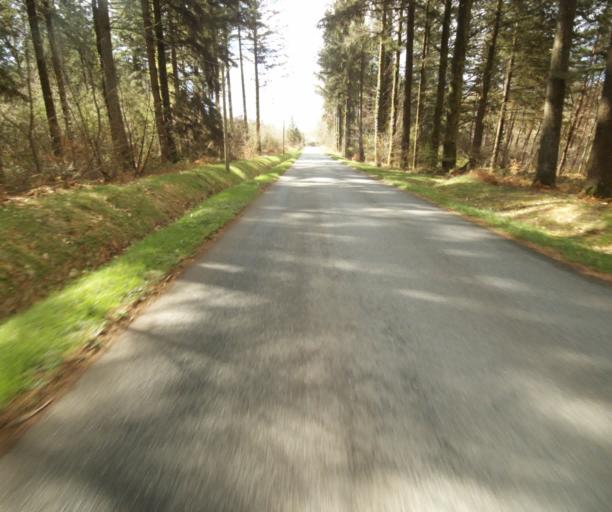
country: FR
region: Limousin
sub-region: Departement de la Correze
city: Argentat
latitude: 45.2293
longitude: 1.9344
